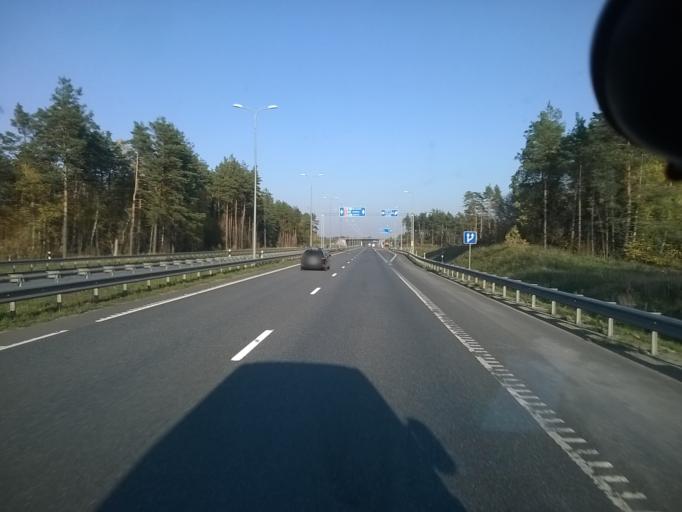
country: EE
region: Harju
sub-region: Kiili vald
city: Kiili
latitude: 59.3181
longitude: 24.7568
